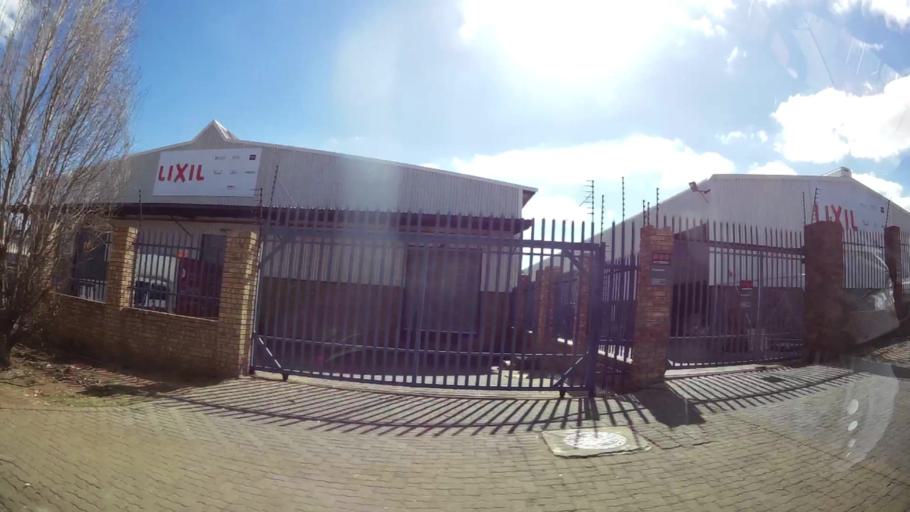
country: ZA
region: Gauteng
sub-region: West Rand District Municipality
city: Krugersdorp
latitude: -26.1177
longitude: 27.8113
